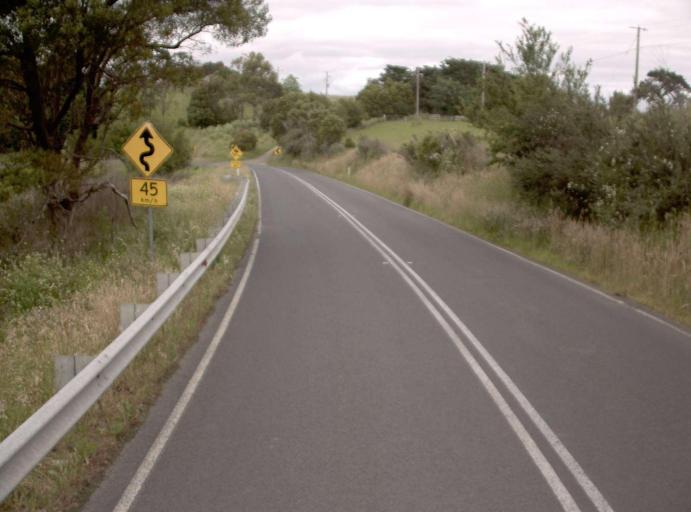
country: AU
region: Victoria
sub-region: Bass Coast
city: North Wonthaggi
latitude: -38.5062
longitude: 145.7237
